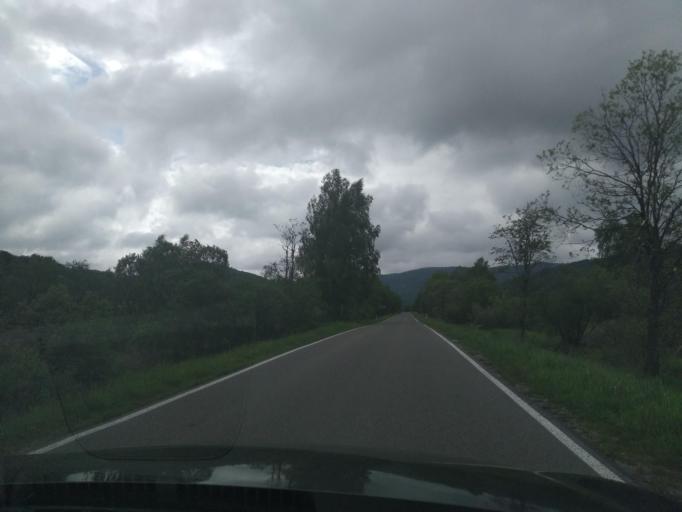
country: PL
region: Subcarpathian Voivodeship
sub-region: Powiat bieszczadzki
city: Lutowiska
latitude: 49.1023
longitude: 22.6483
